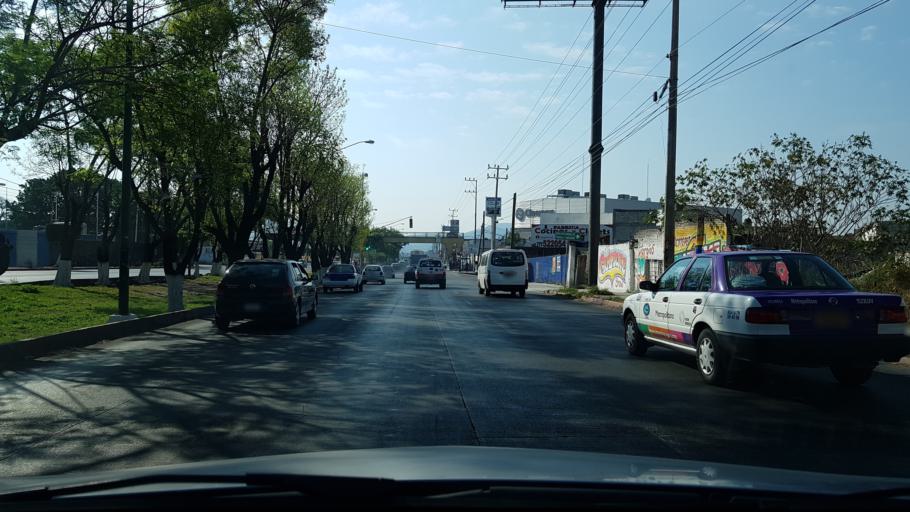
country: MX
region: Morelos
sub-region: Tepoztlan
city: Tetecolala
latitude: 18.9057
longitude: -99.1776
